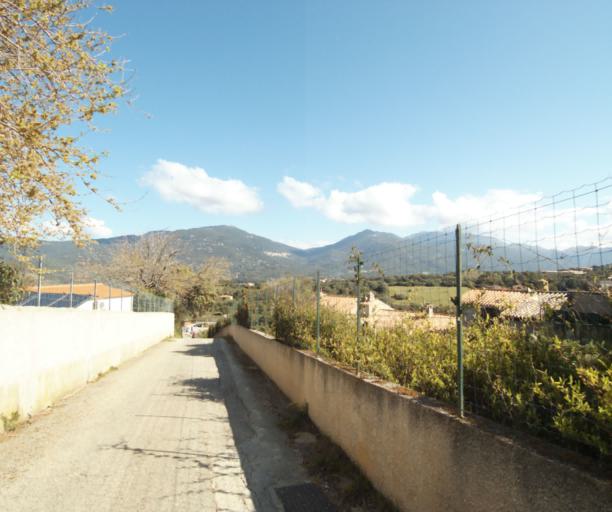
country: FR
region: Corsica
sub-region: Departement de la Corse-du-Sud
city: Propriano
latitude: 41.6692
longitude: 8.9094
